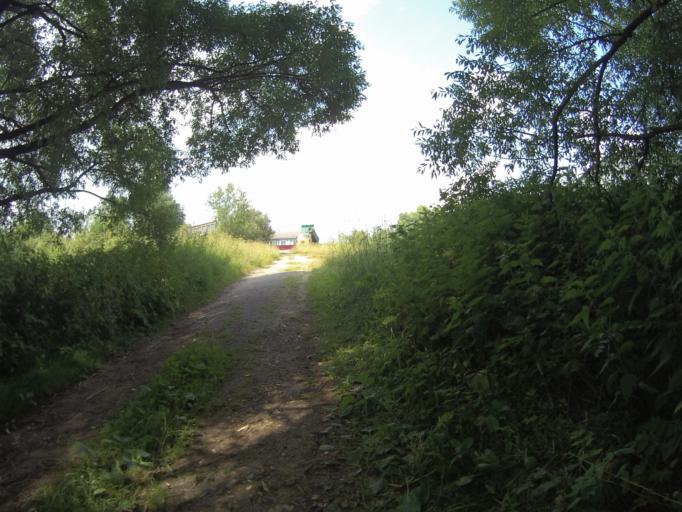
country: RU
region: Vladimir
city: Kommunar
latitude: 56.0760
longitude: 40.5522
